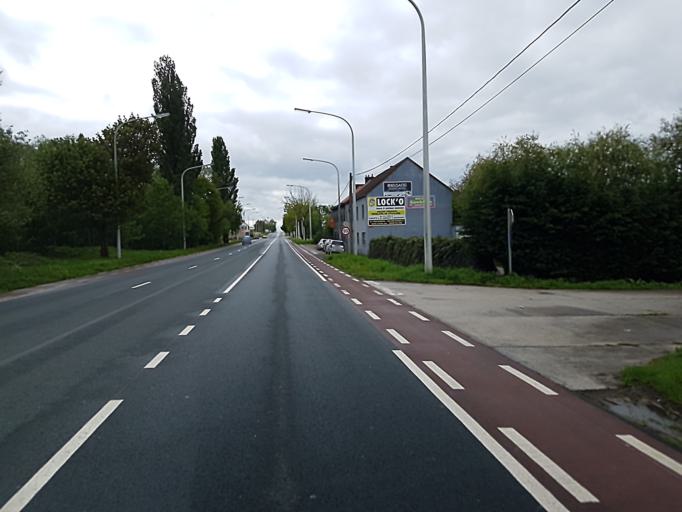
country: BE
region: Wallonia
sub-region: Province du Brabant Wallon
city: Chastre-Villeroux-Blanmont
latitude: 50.6172
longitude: 4.6630
